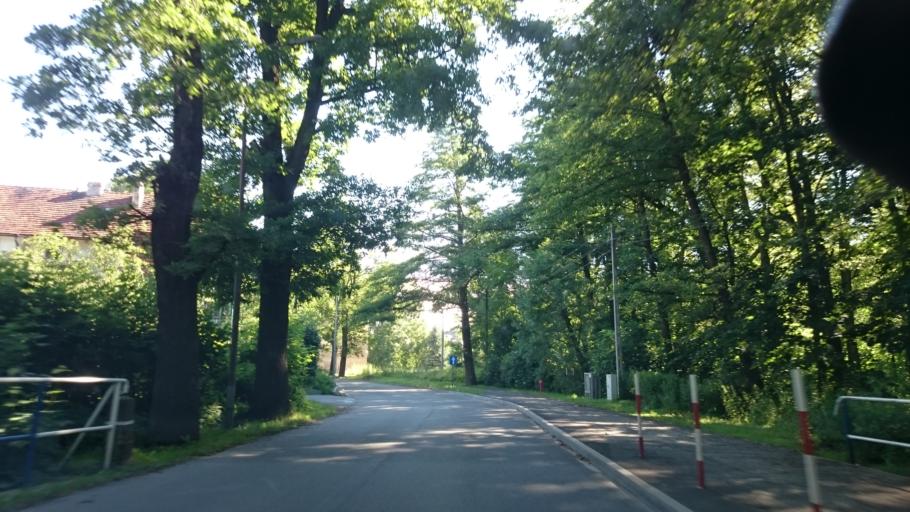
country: PL
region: Lower Silesian Voivodeship
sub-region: Powiat klodzki
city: Bystrzyca Klodzka
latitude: 50.2914
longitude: 16.6463
